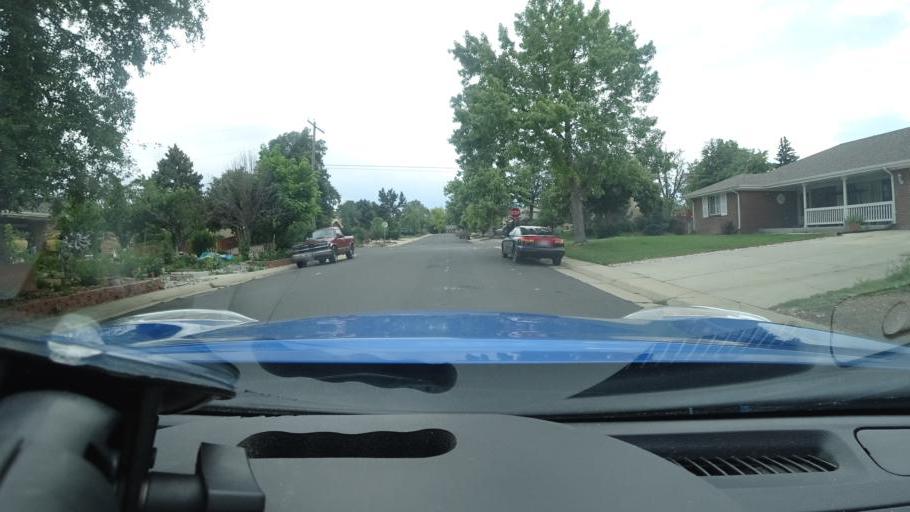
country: US
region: Colorado
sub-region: Adams County
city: Aurora
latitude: 39.7224
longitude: -104.8343
